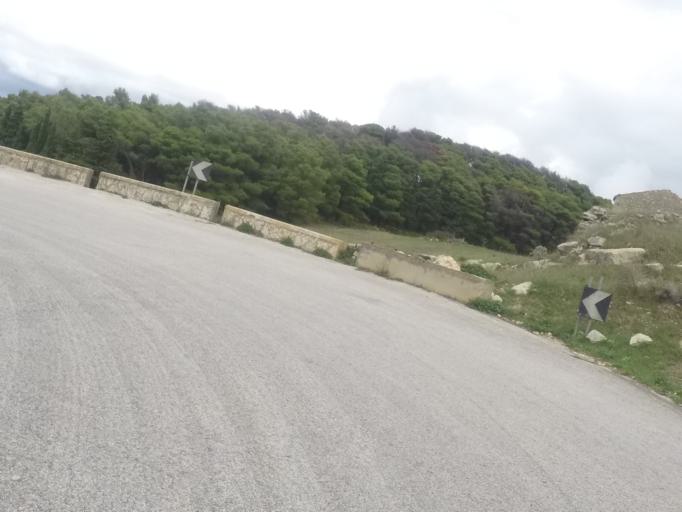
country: IT
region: Sicily
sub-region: Trapani
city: Erice
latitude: 38.0428
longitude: 12.5831
